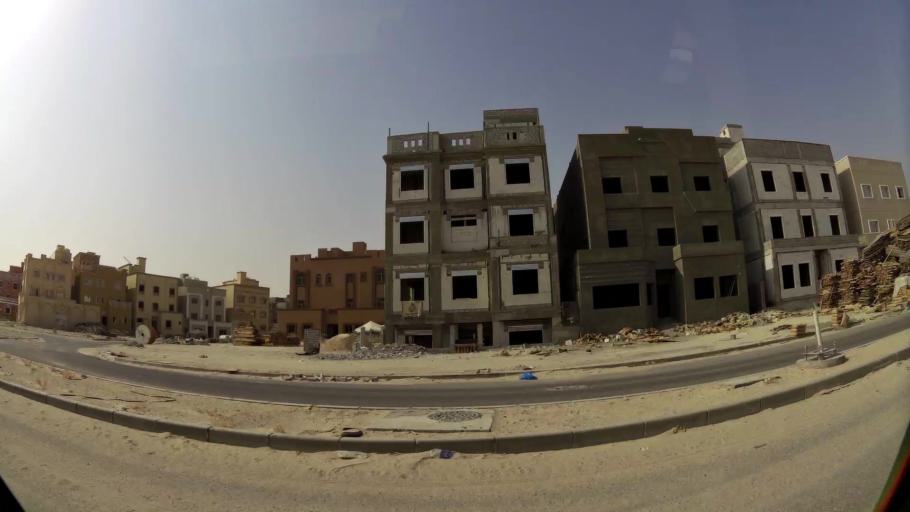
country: KW
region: Muhafazat al Jahra'
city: Al Jahra'
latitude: 29.3578
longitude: 47.7493
